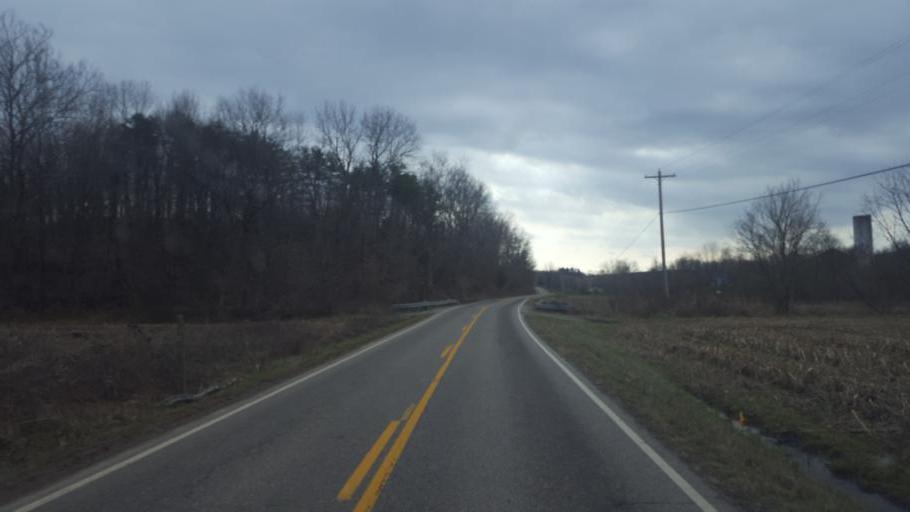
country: US
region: Ohio
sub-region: Gallia County
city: Gallipolis
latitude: 38.7417
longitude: -82.3680
